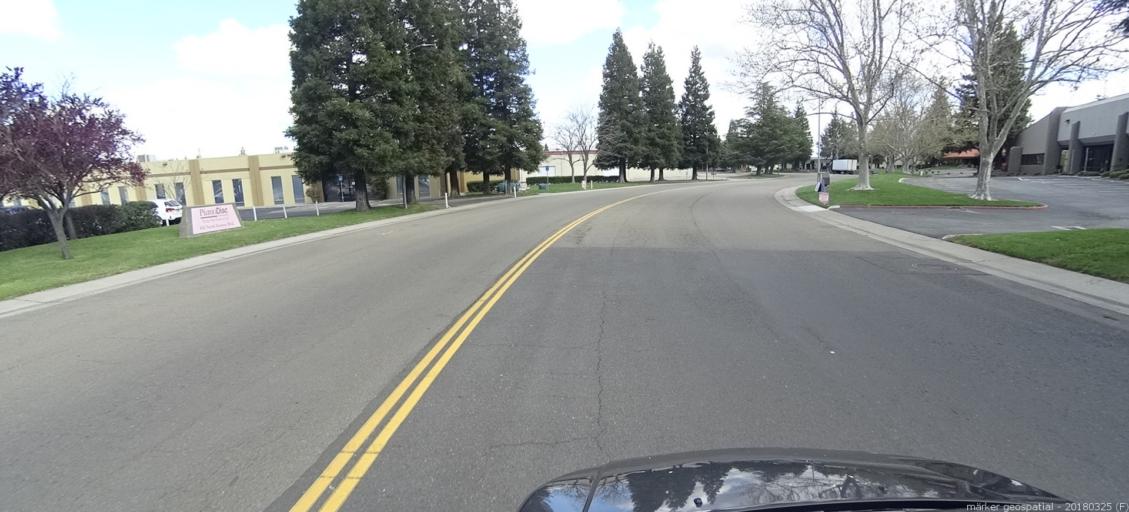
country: US
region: California
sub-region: Sacramento County
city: Rio Linda
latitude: 38.6436
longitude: -121.4790
